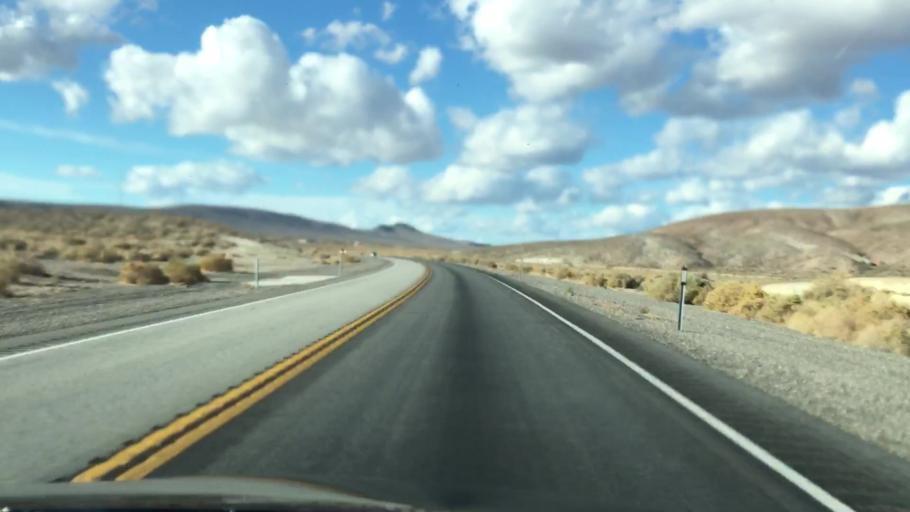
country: US
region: Nevada
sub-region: Nye County
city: Beatty
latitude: 37.0335
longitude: -116.7590
